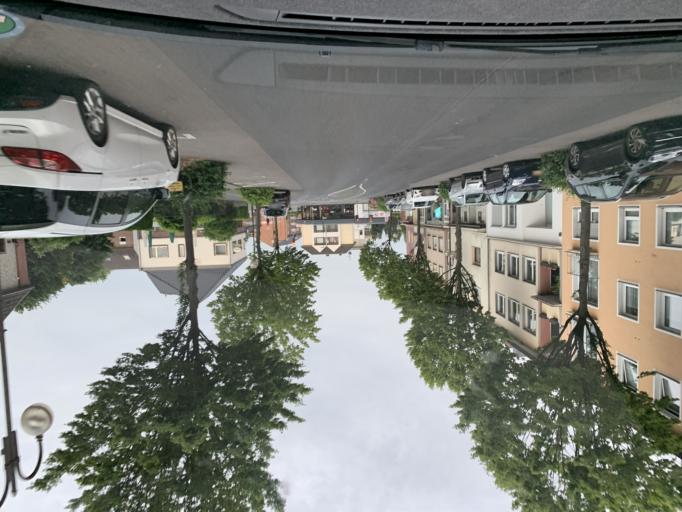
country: DE
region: North Rhine-Westphalia
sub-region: Regierungsbezirk Koln
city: Kerpen
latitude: 50.9099
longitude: 6.7118
